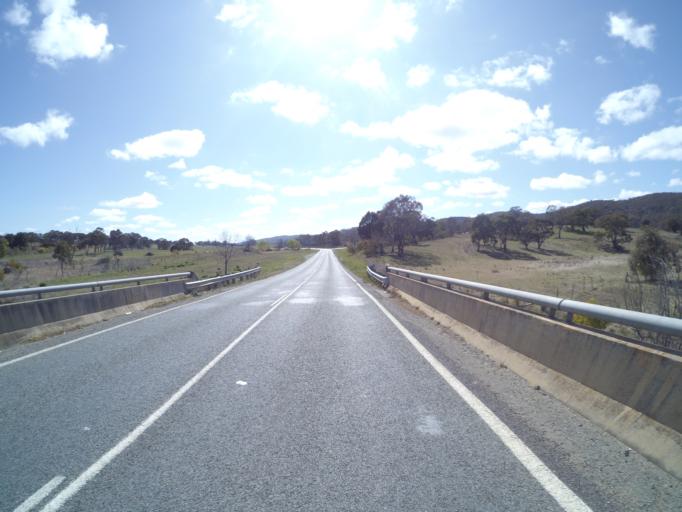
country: AU
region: New South Wales
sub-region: Queanbeyan
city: Queanbeyan
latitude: -35.3216
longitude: 149.2419
